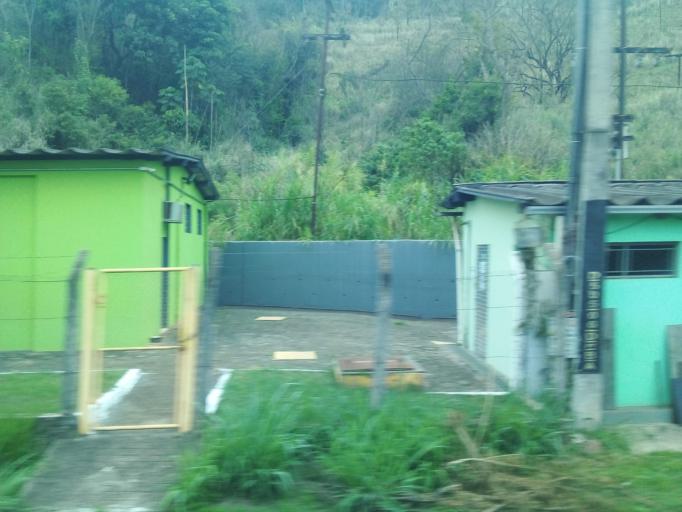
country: BR
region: Minas Gerais
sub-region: Nova Era
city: Nova Era
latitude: -19.7290
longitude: -43.0071
